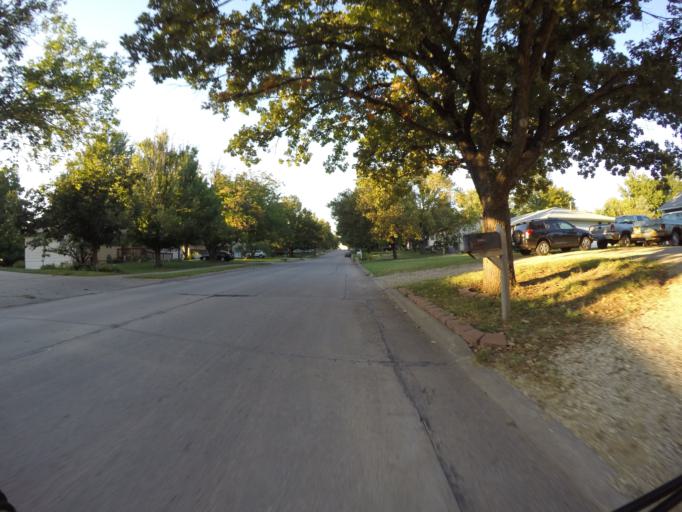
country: US
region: Kansas
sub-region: Riley County
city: Manhattan
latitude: 39.1932
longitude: -96.6167
